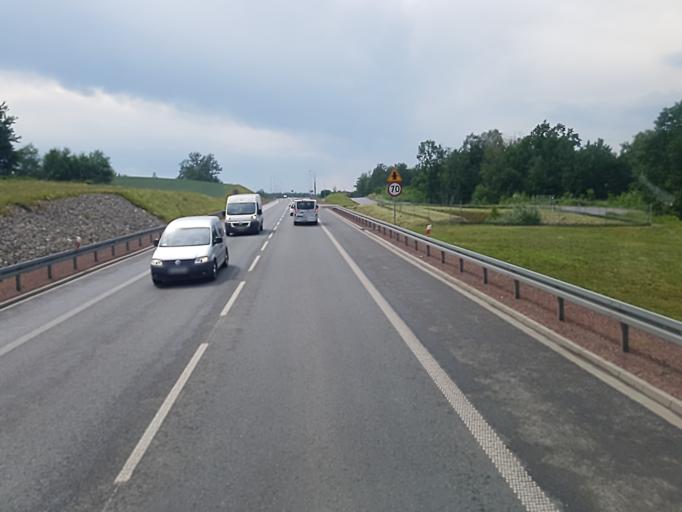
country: PL
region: Silesian Voivodeship
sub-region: Jastrzebie-Zdroj
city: Jastrzebie Zdroj
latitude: 49.9724
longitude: 18.5727
